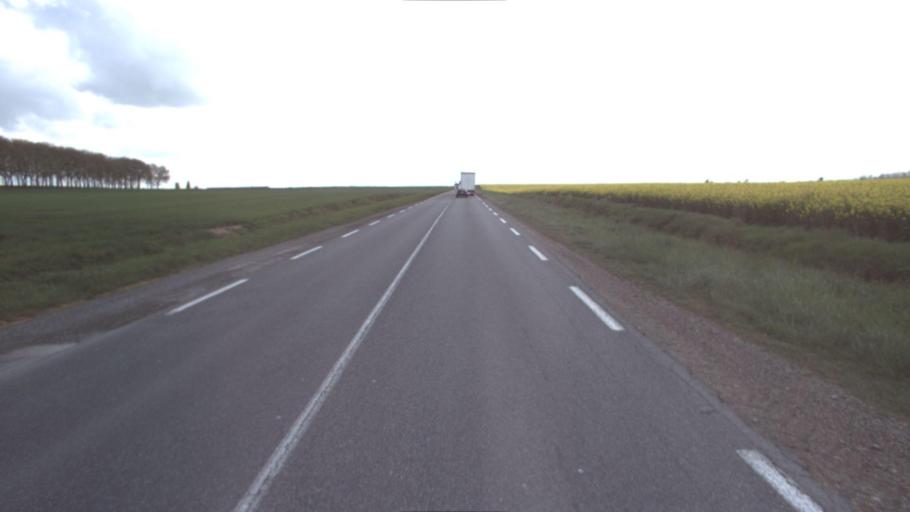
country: FR
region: Ile-de-France
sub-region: Departement de Seine-et-Marne
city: Villiers-Saint-Georges
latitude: 48.6919
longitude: 3.3295
